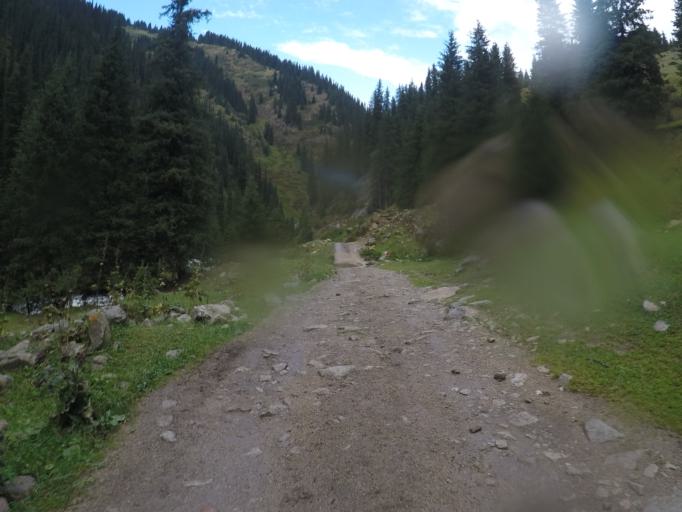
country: KG
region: Ysyk-Koel
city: Teploklyuchenka
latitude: 42.4133
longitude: 78.5736
